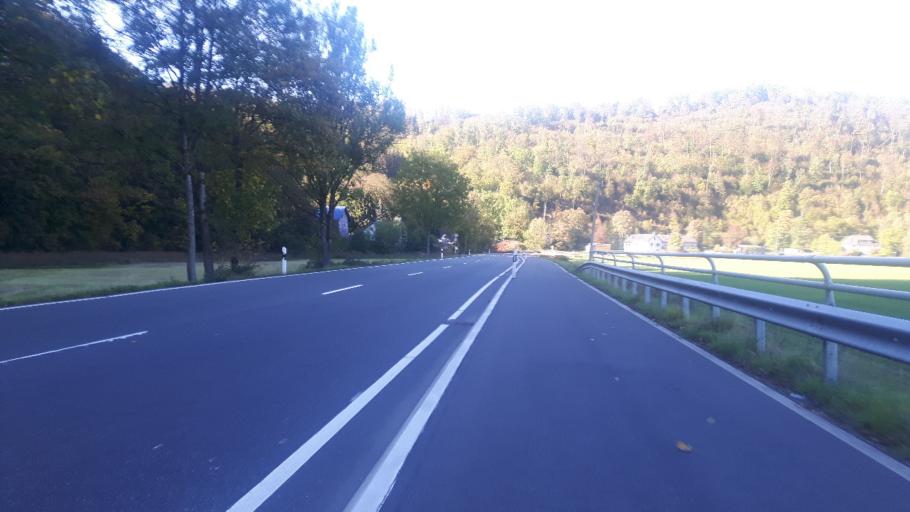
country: DE
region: Rheinland-Pfalz
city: Mittelhof
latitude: 50.7996
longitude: 7.7863
